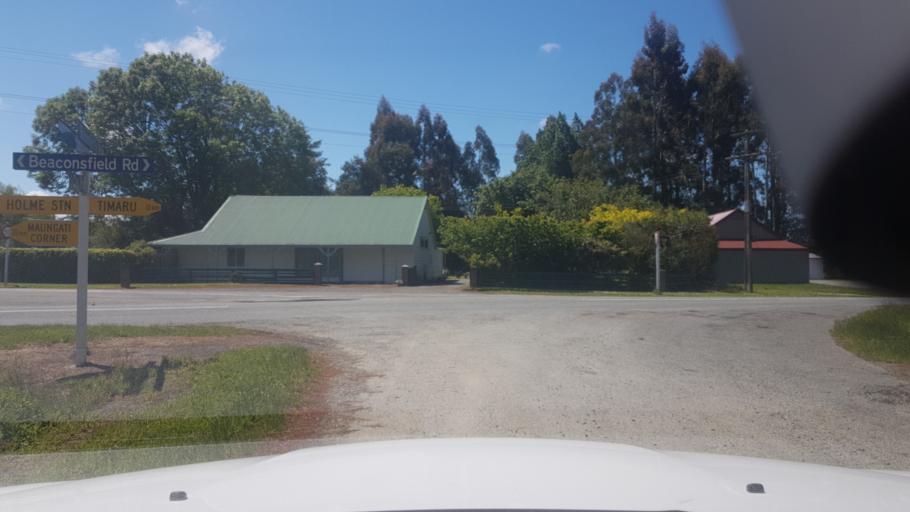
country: NZ
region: Canterbury
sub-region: Timaru District
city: Timaru
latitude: -44.4398
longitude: 171.1626
